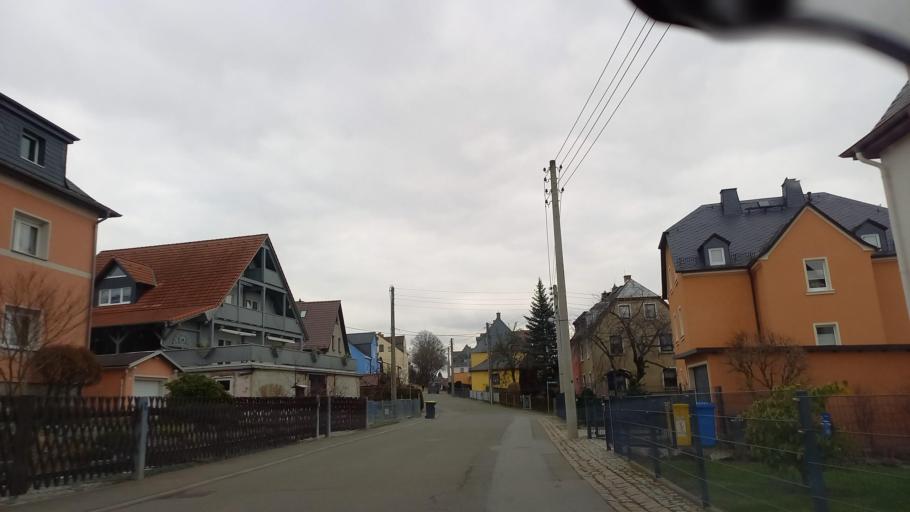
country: DE
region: Saxony
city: Wilkau-Hasslau
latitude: 50.6795
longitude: 12.5137
